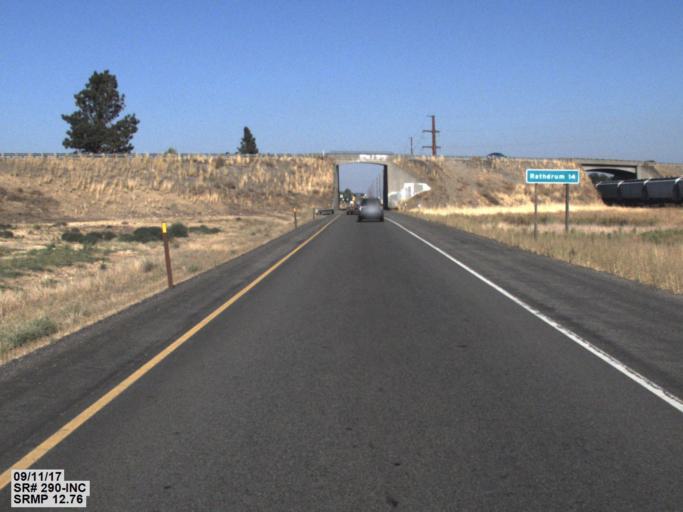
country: US
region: Washington
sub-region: Spokane County
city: Liberty Lake
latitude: 47.7009
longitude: -117.1500
